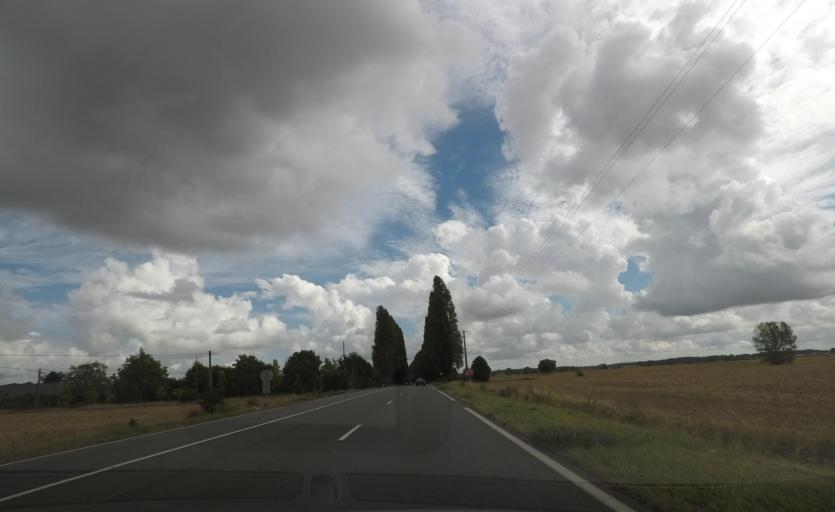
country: FR
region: Pays de la Loire
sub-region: Departement de Maine-et-Loire
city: Villeveque
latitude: 47.5352
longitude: -0.4116
